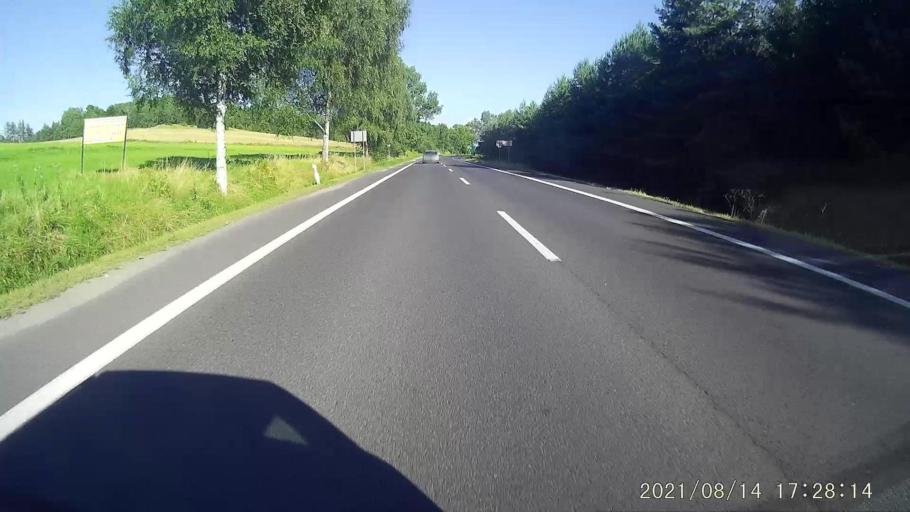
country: PL
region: Lower Silesian Voivodeship
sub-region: Jelenia Gora
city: Jelenia Gora
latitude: 50.9132
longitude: 15.6880
